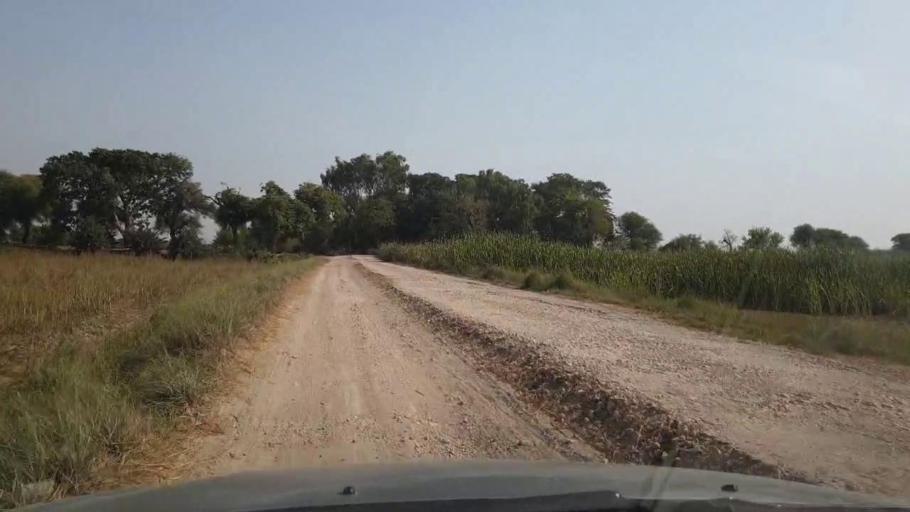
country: PK
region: Sindh
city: Bulri
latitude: 24.9063
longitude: 68.3739
